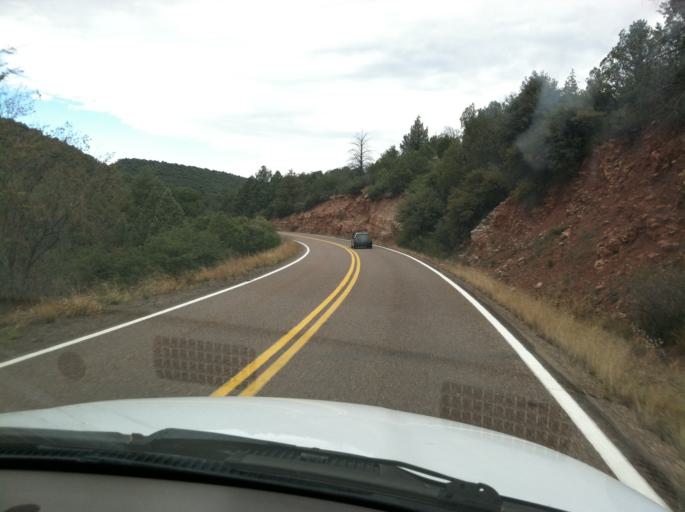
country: US
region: Arizona
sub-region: Gila County
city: Payson
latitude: 34.3134
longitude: -111.3688
